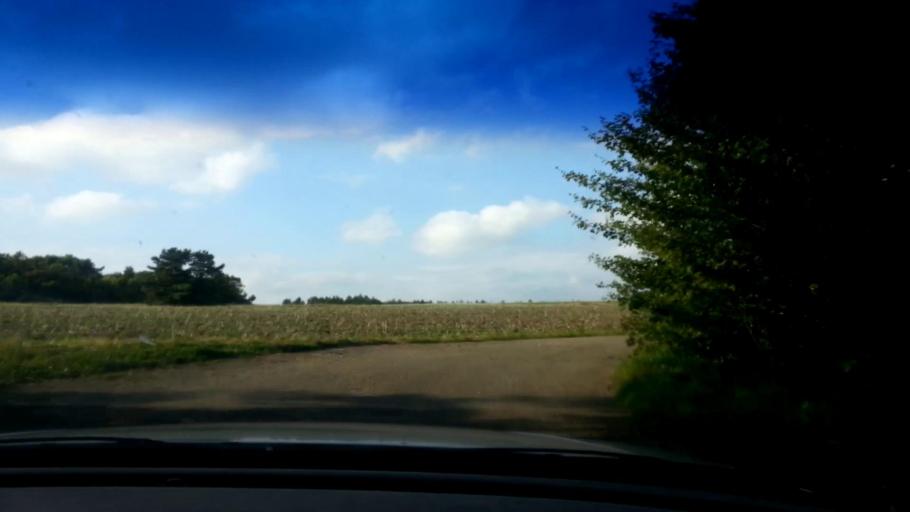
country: DE
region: Bavaria
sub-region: Upper Franconia
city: Schesslitz
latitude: 50.0174
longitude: 11.0342
